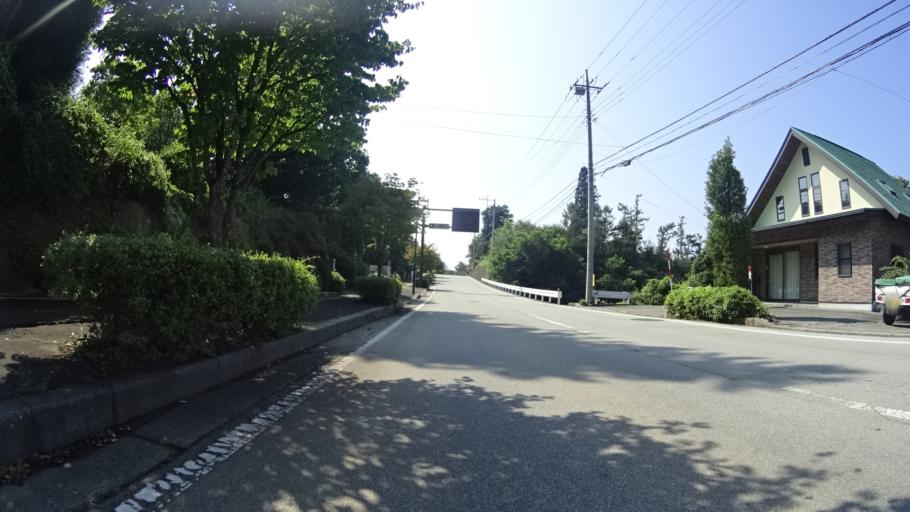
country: JP
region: Nagano
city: Chino
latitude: 35.8680
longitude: 138.2993
